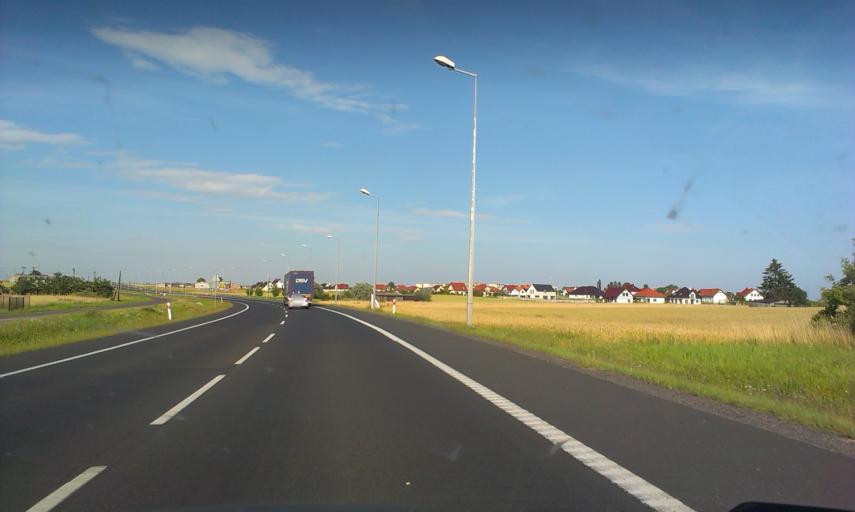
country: PL
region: Kujawsko-Pomorskie
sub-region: Powiat nakielski
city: Naklo nad Notecia
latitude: 53.1438
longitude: 17.5693
